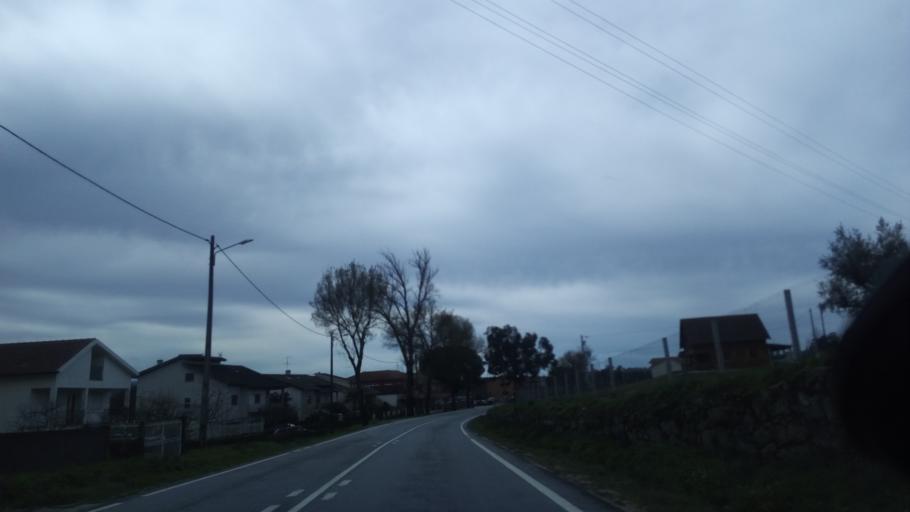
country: PT
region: Guarda
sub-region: Seia
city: Seia
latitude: 40.4608
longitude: -7.6901
